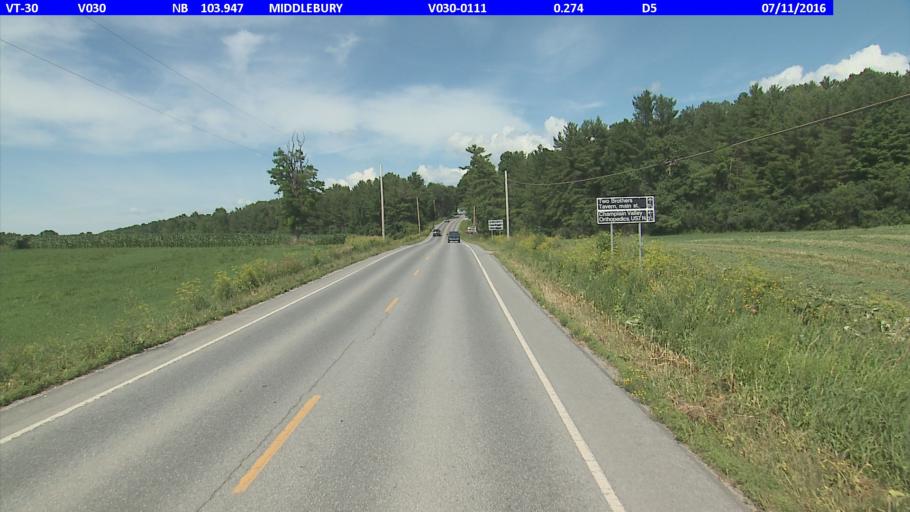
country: US
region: Vermont
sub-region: Addison County
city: Middlebury (village)
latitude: 43.9982
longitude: -73.1865
